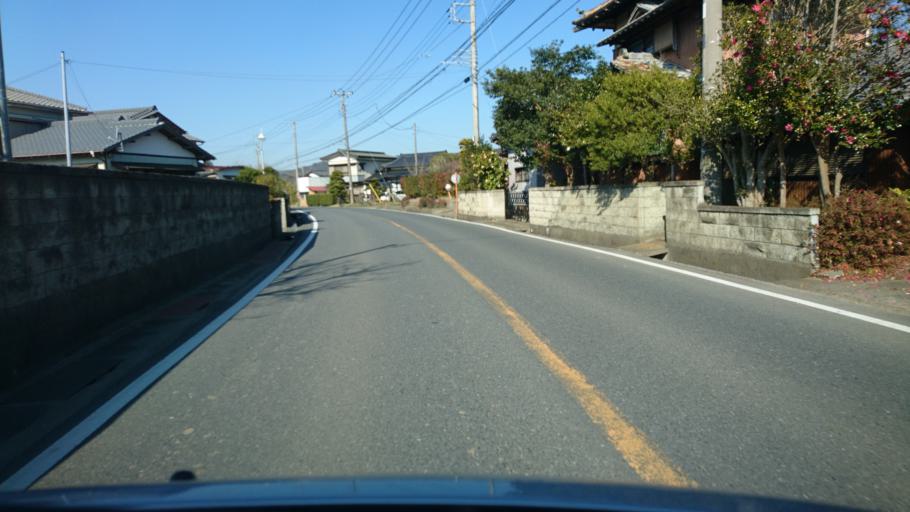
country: JP
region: Chiba
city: Kimitsu
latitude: 35.3004
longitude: 139.9750
